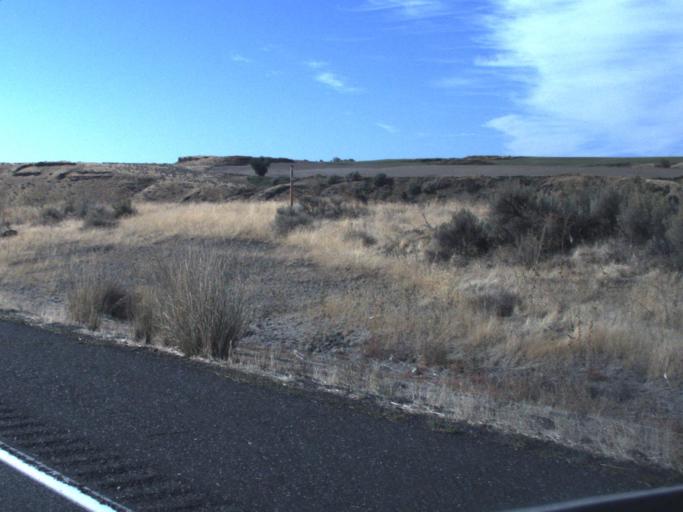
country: US
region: Washington
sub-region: Franklin County
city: Basin City
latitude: 46.5023
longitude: -119.0151
